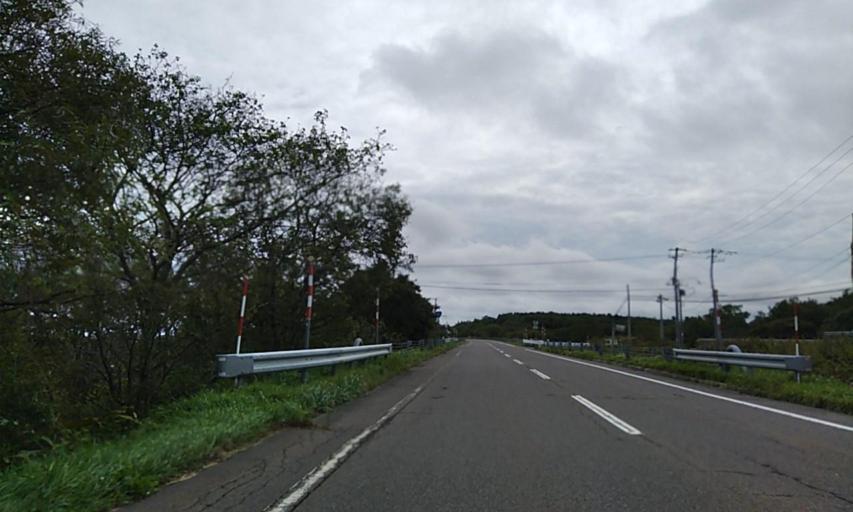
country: JP
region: Hokkaido
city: Shibetsu
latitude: 43.5444
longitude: 145.2305
